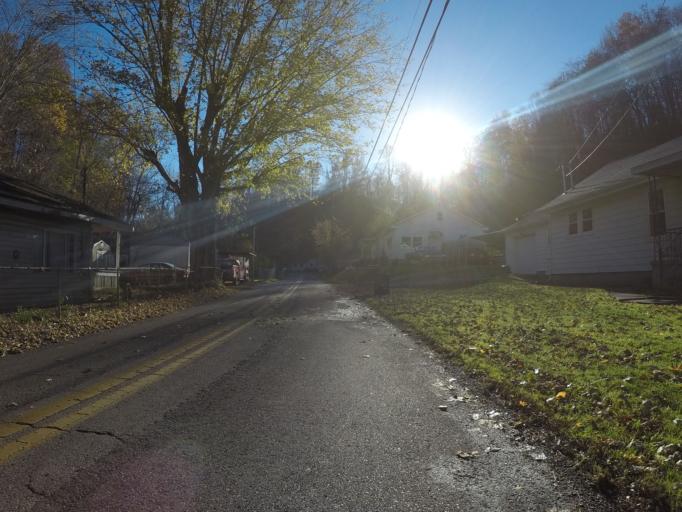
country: US
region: West Virginia
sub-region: Wayne County
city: Kenova
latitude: 38.3902
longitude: -82.5707
